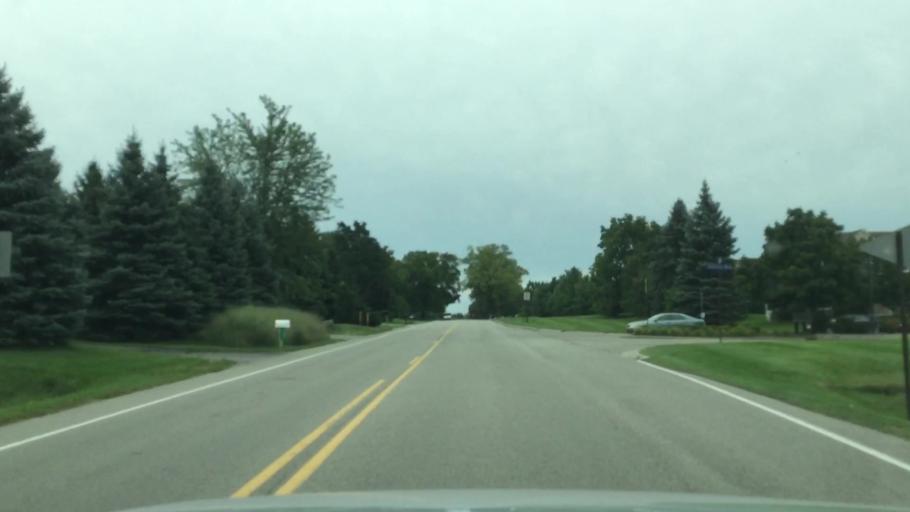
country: US
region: Michigan
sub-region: Washtenaw County
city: Ypsilanti
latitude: 42.2065
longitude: -83.6599
